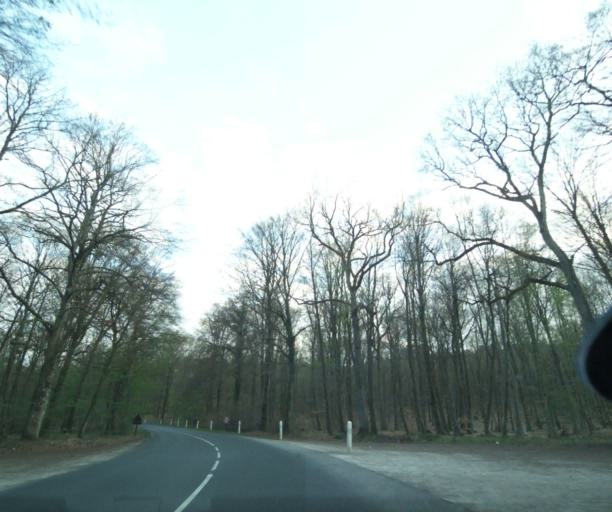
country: FR
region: Ile-de-France
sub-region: Departement de Seine-et-Marne
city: Montigny-sur-Loing
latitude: 48.3561
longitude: 2.7614
